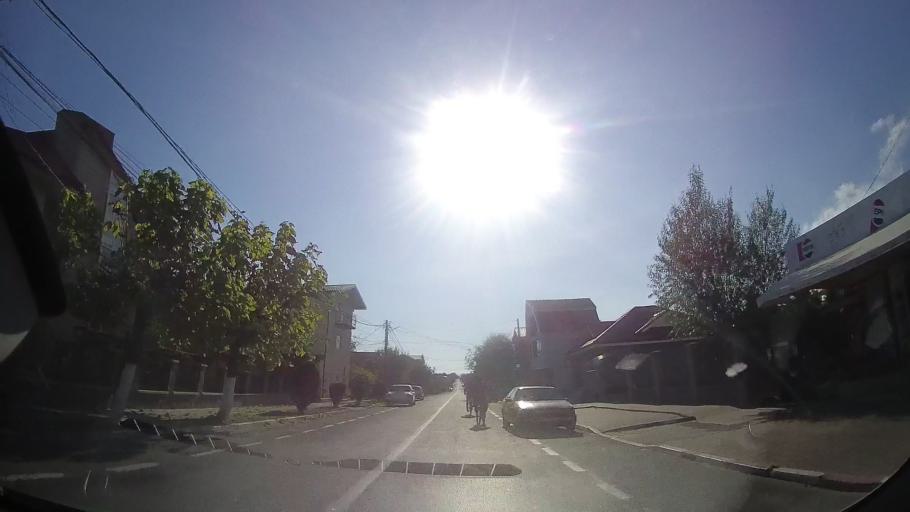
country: RO
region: Constanta
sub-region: Comuna Costinesti
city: Schitu
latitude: 43.9460
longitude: 28.6300
